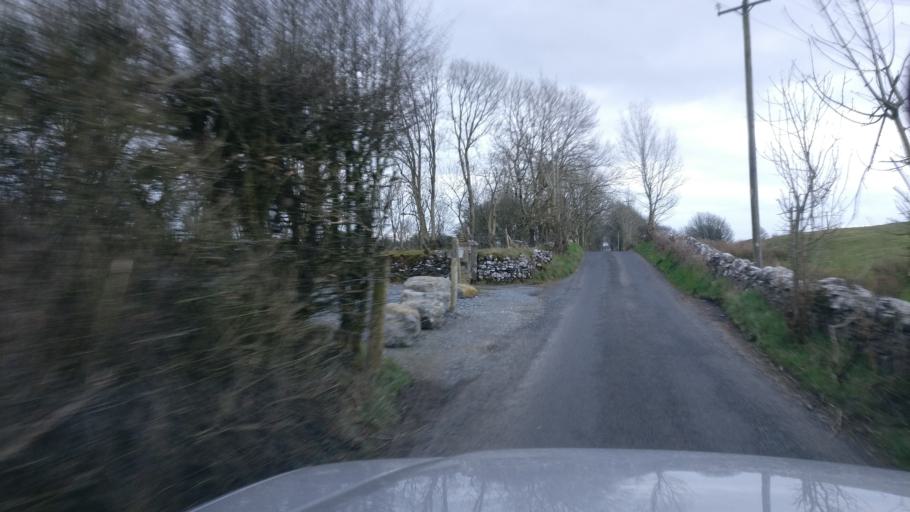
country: IE
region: Connaught
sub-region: County Galway
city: Loughrea
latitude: 53.2599
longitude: -8.4511
